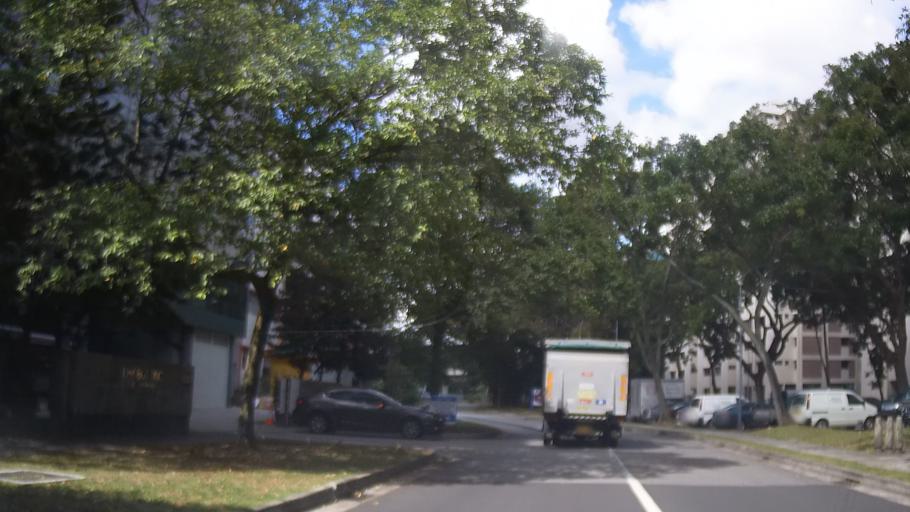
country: SG
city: Singapore
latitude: 1.3188
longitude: 103.8775
